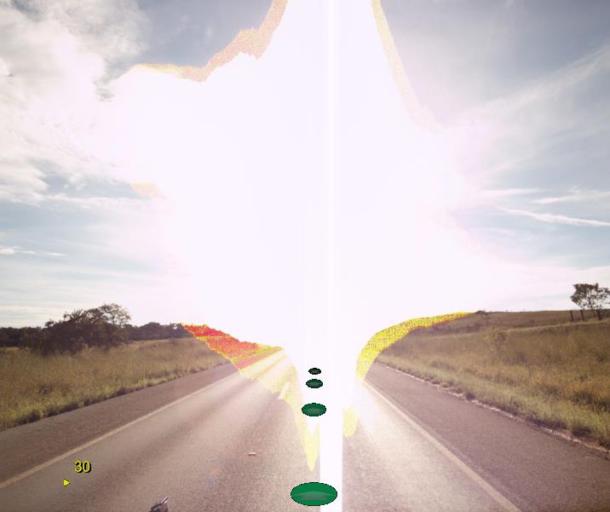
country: BR
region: Goias
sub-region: Abadiania
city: Abadiania
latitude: -15.7675
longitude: -48.4517
